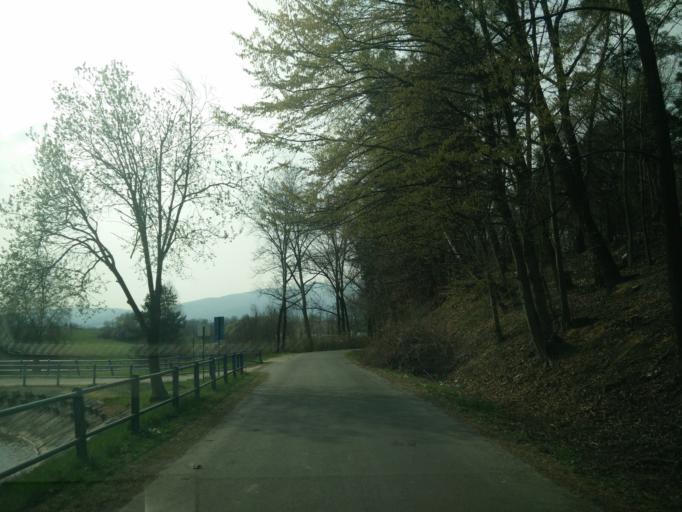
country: SK
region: Nitriansky
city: Prievidza
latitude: 48.8229
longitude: 18.6659
